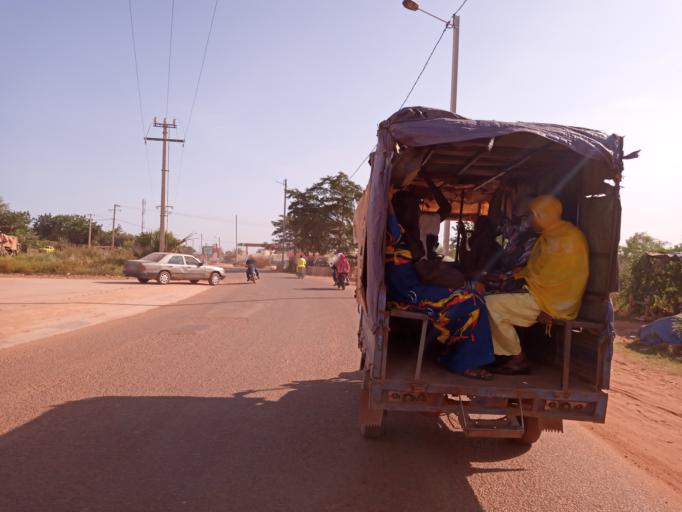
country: ML
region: Bamako
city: Bamako
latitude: 12.6249
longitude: -7.9553
